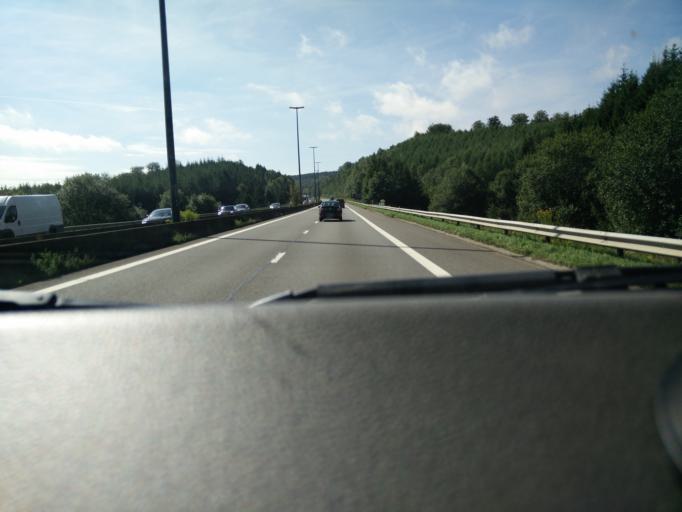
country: BE
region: Wallonia
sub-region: Province du Luxembourg
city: Tellin
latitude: 50.0295
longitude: 5.2106
